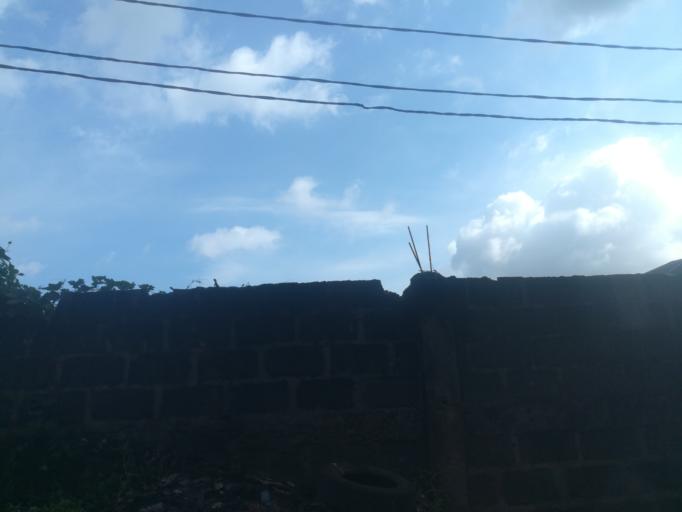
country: NG
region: Lagos
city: Somolu
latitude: 6.5574
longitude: 3.3841
